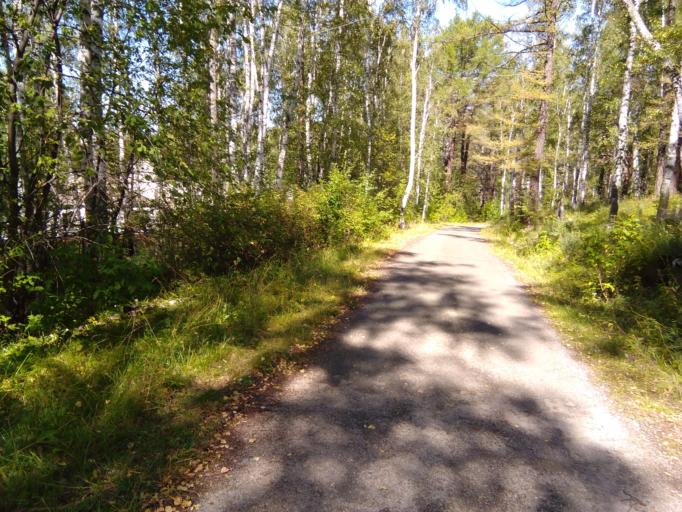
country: RU
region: Bashkortostan
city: Abzakovo
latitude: 53.8135
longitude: 58.6032
